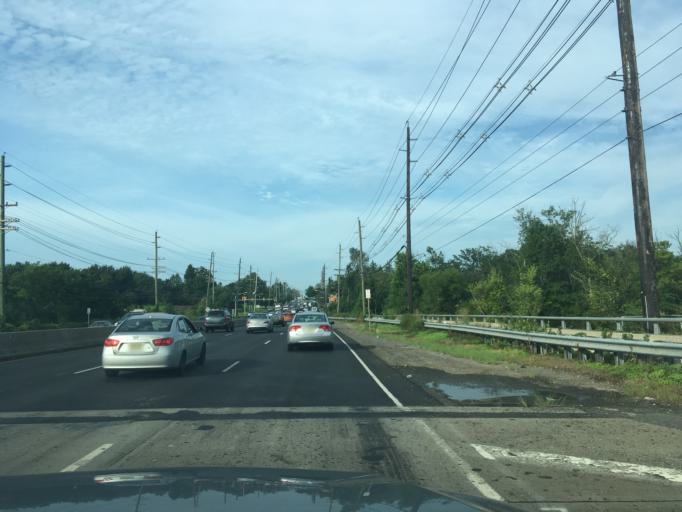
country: US
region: New Jersey
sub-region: Mercer County
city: Princeton Junction
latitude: 40.3388
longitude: -74.6294
